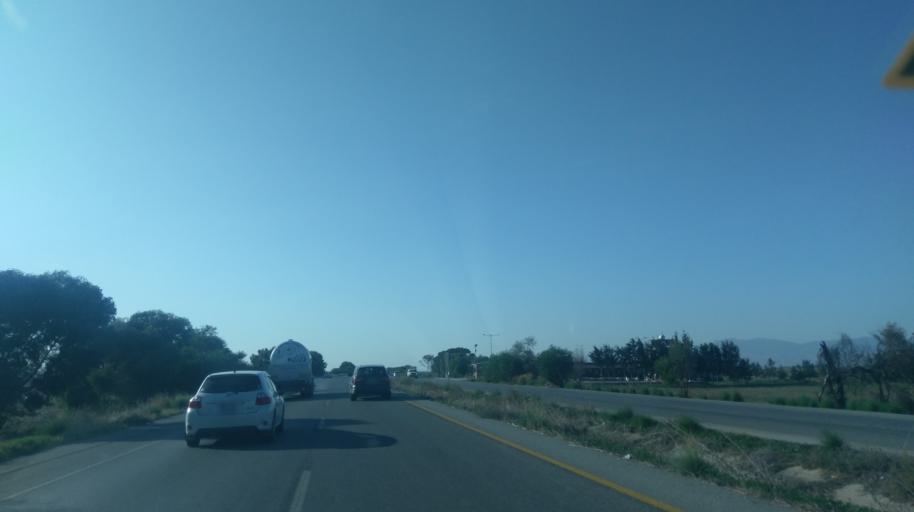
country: CY
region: Ammochostos
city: Lefkonoiko
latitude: 35.1803
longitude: 33.7226
